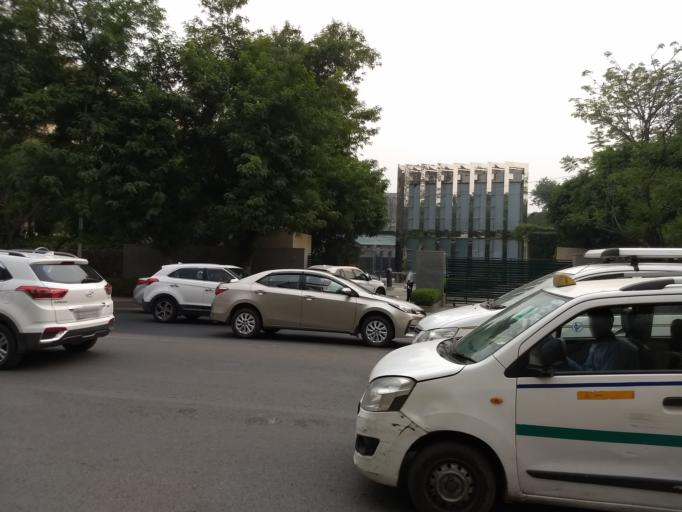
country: IN
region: Haryana
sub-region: Gurgaon
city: Gurgaon
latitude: 28.5029
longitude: 77.0889
